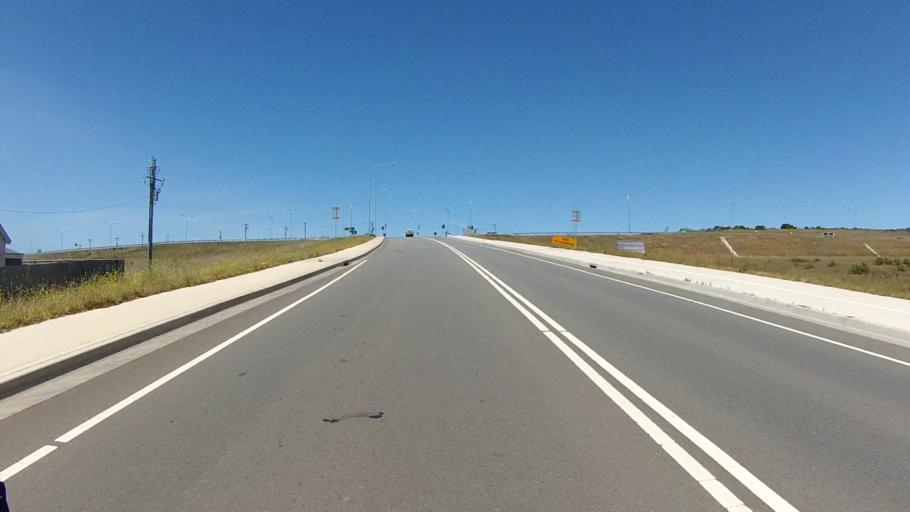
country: AU
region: Tasmania
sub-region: Clarence
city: Howrah
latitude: -42.8873
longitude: 147.4286
